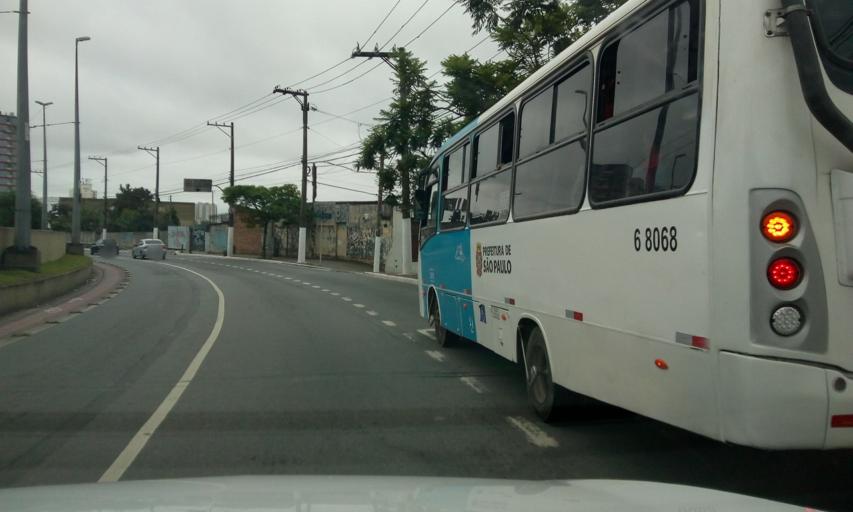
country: BR
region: Sao Paulo
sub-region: Diadema
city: Diadema
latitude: -23.6585
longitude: -46.6358
